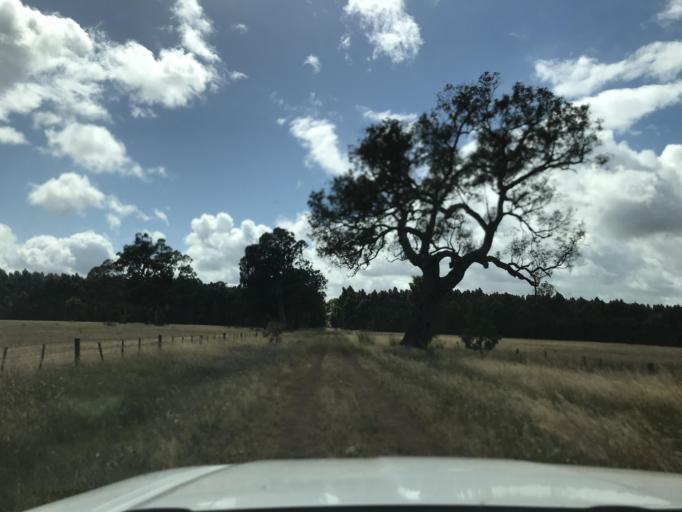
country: AU
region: South Australia
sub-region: Wattle Range
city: Penola
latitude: -37.1914
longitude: 141.3936
